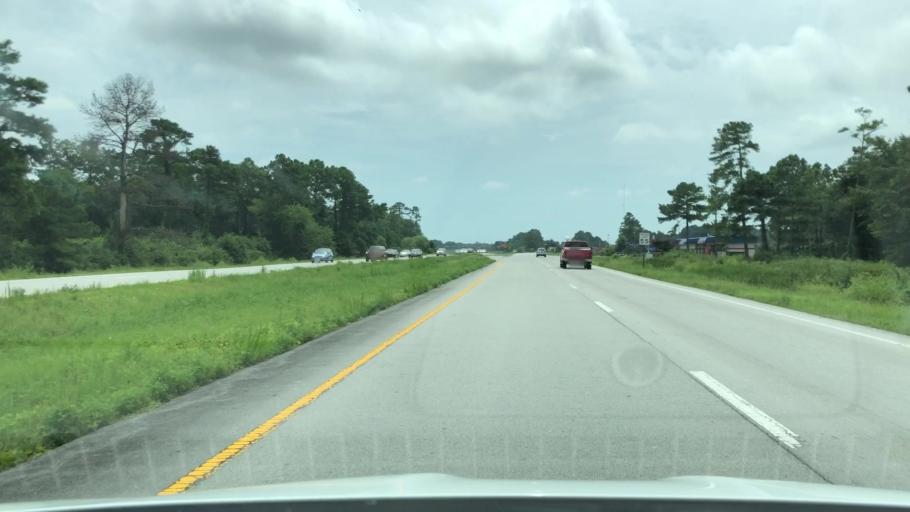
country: US
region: North Carolina
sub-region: Carteret County
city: Newport
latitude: 34.7952
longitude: -76.8776
